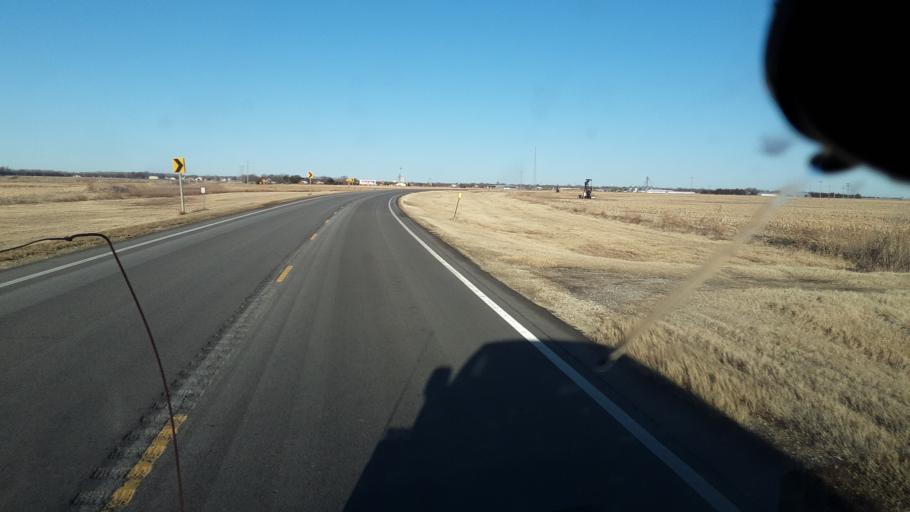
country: US
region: Kansas
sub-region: Barton County
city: Ellinwood
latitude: 38.3459
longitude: -98.5502
